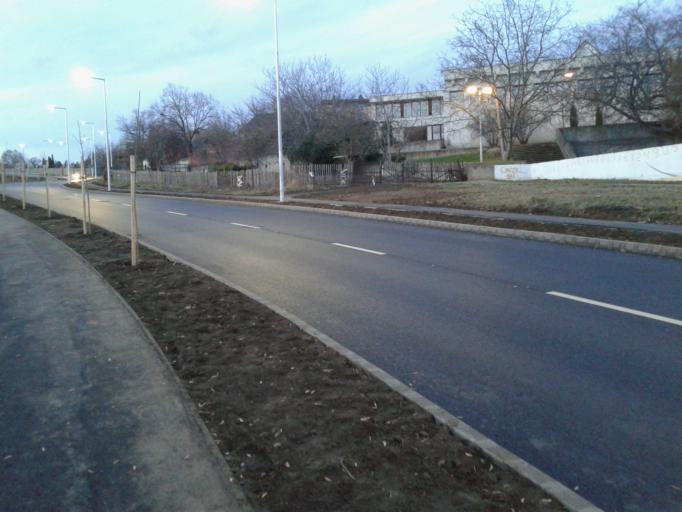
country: HU
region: Baranya
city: Pecs
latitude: 46.0780
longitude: 18.2138
